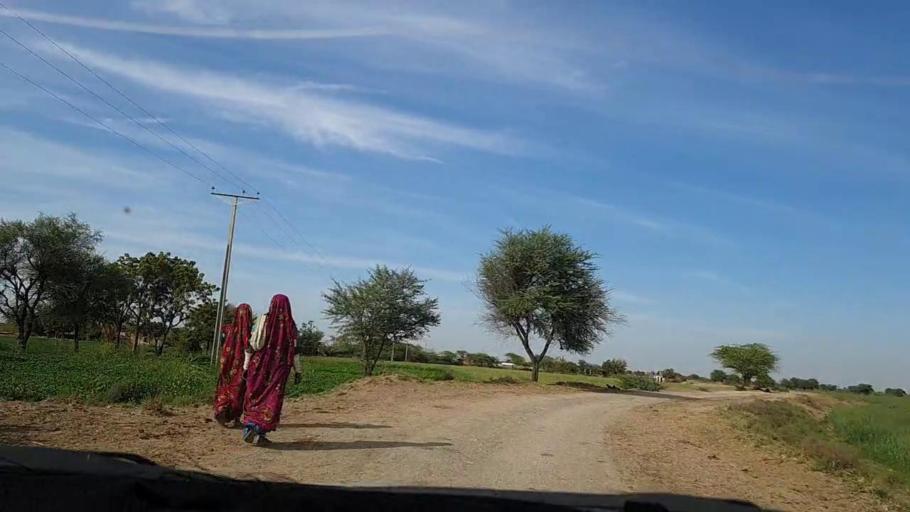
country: PK
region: Sindh
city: Dhoro Naro
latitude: 25.4799
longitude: 69.5405
